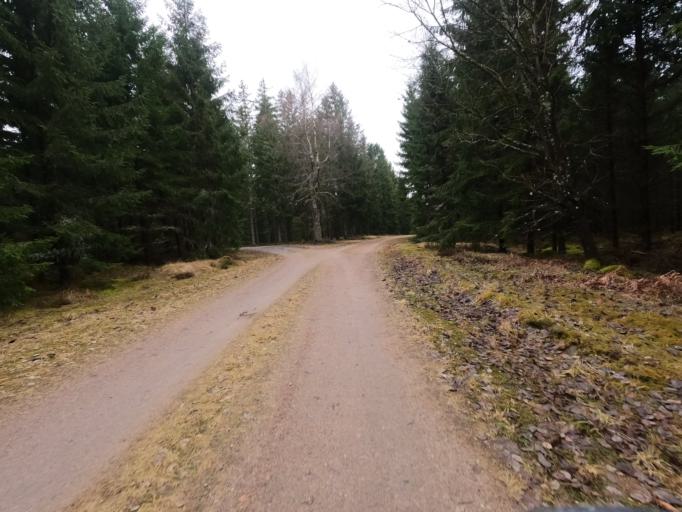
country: SE
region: Kronoberg
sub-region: Markaryds Kommun
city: Stromsnasbruk
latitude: 56.8083
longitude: 13.5706
